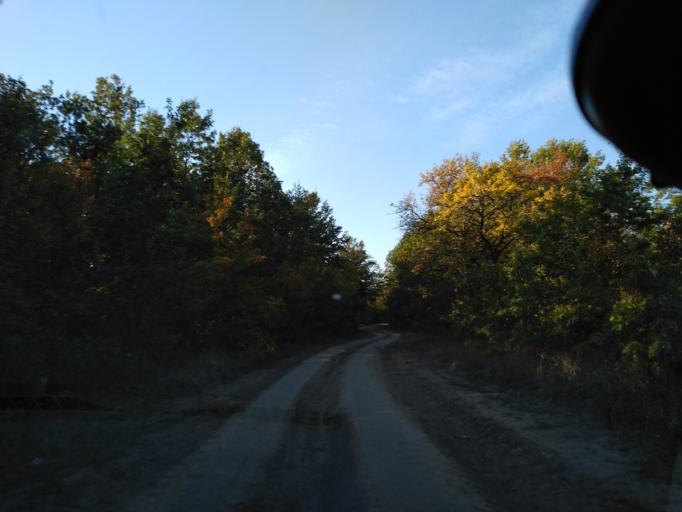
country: RO
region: Timis
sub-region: Comuna Bogda
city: Bogda
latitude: 45.9026
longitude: 21.5738
